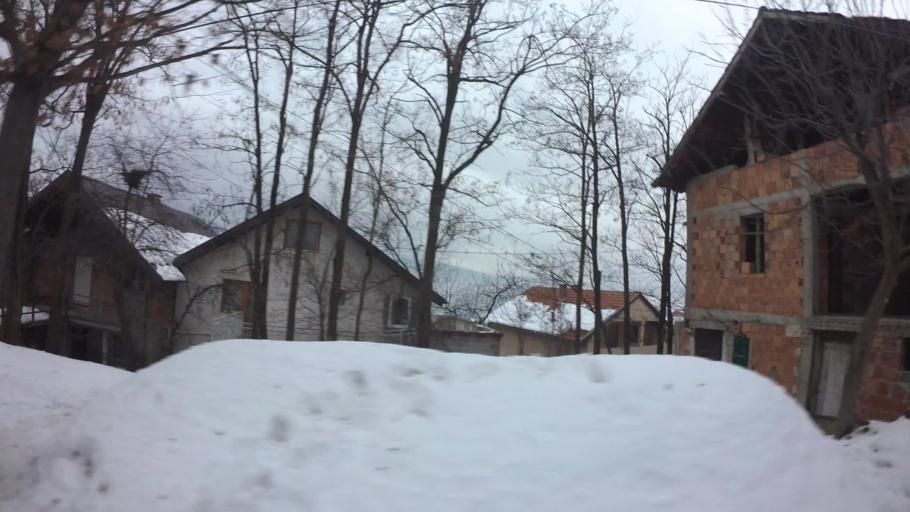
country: BA
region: Federation of Bosnia and Herzegovina
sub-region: Kanton Sarajevo
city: Sarajevo
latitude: 43.8569
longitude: 18.3527
